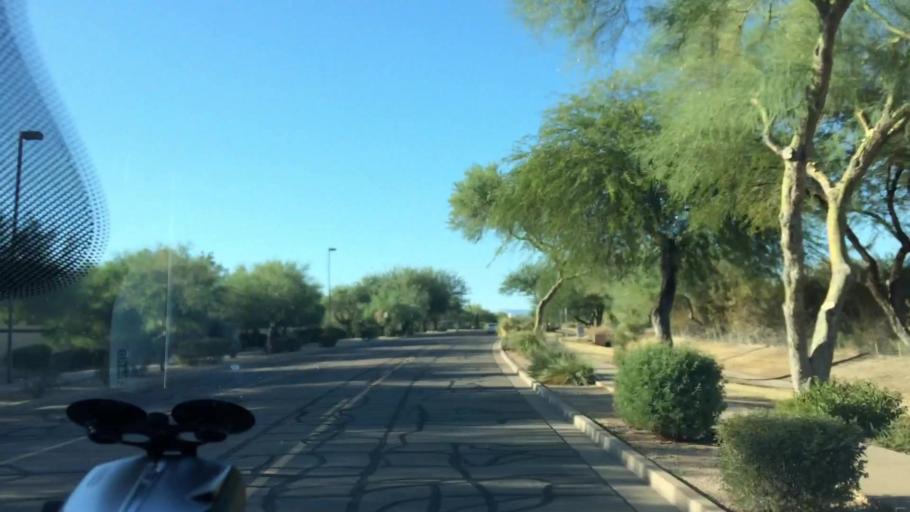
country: US
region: Arizona
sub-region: Maricopa County
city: Paradise Valley
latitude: 33.6472
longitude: -111.9032
